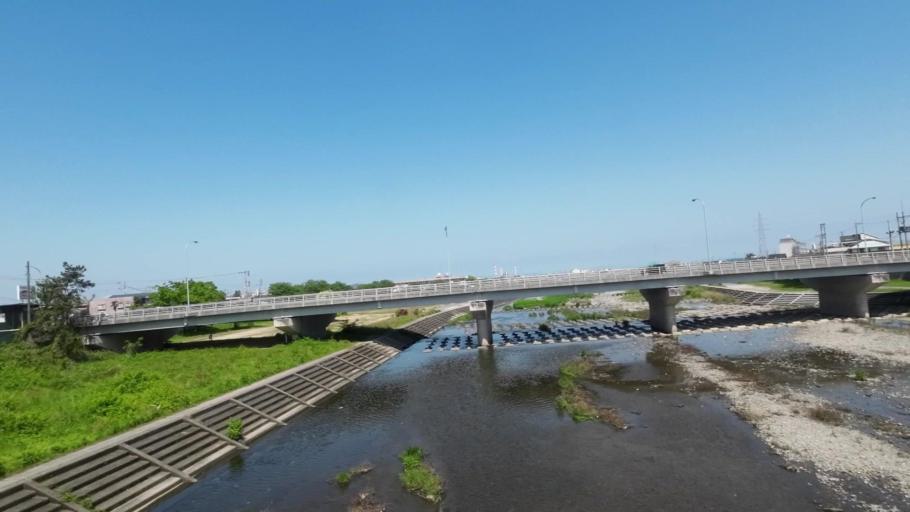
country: JP
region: Ehime
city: Niihama
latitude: 33.9547
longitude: 133.3023
